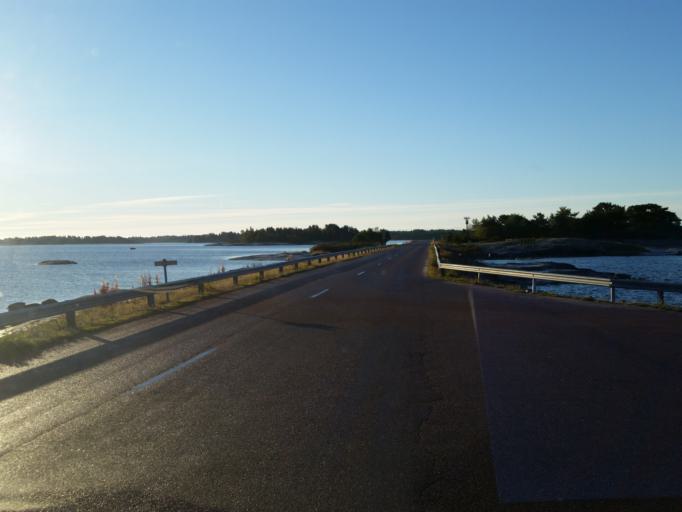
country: AX
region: Alands skaergard
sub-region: Vardoe
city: Vardoe
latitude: 60.3220
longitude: 20.3727
